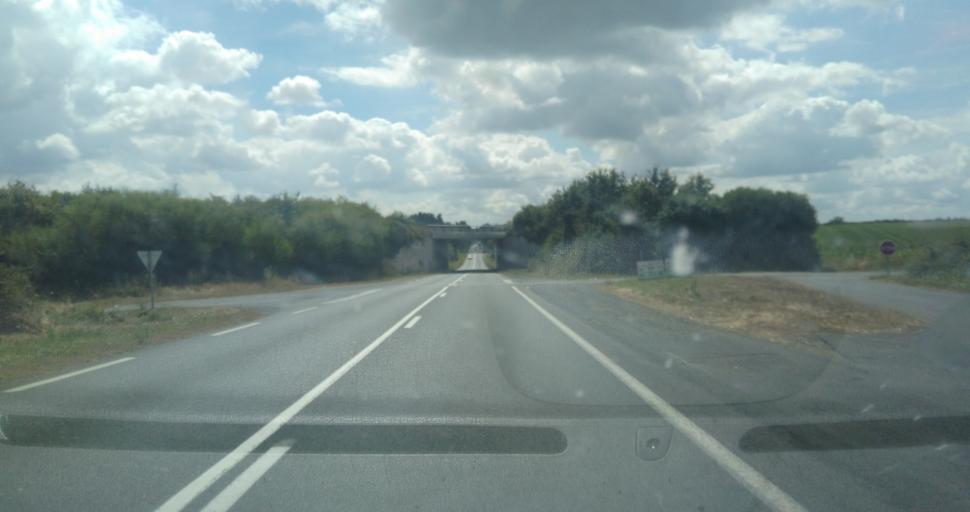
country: FR
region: Pays de la Loire
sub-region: Departement de la Vendee
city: Bournezeau
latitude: 46.6065
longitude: -1.1402
